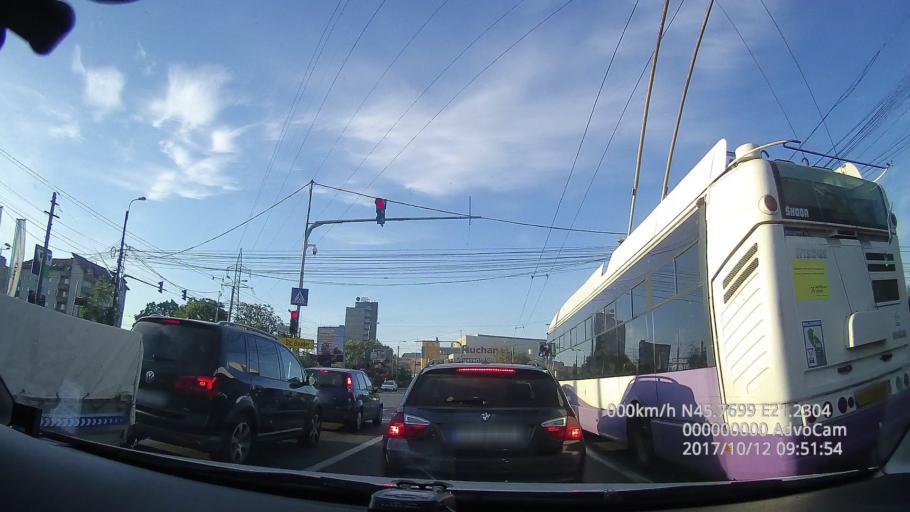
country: RO
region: Timis
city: Timisoara
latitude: 45.7642
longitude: 21.2388
